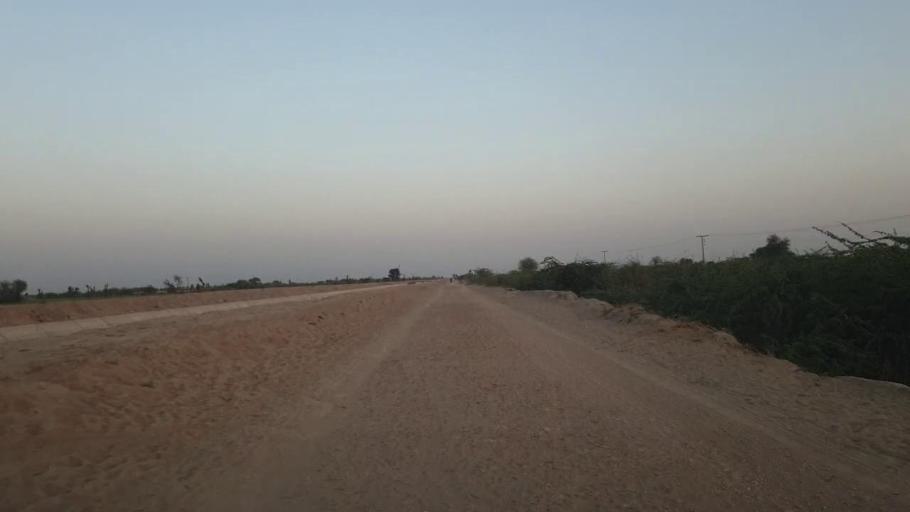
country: PK
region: Sindh
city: Dhoro Naro
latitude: 25.4405
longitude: 69.6371
